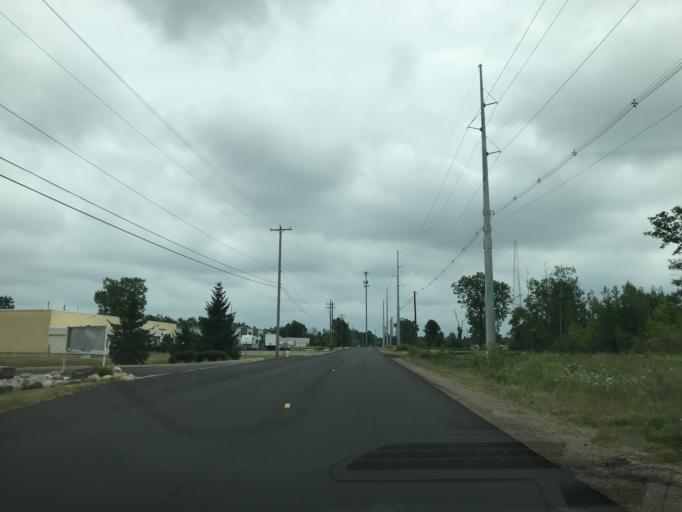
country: US
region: Michigan
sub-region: Eaton County
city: Waverly
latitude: 42.7047
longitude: -84.6288
